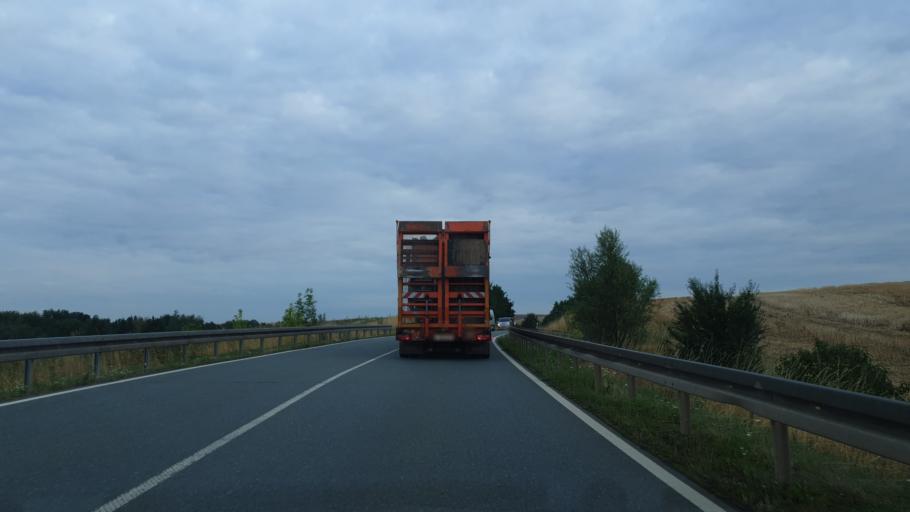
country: DE
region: Saxony
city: Sankt Egidien
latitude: 50.7889
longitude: 12.6302
